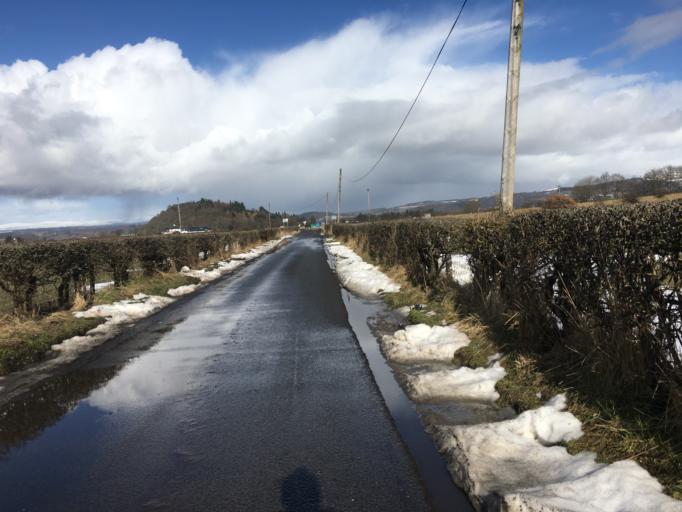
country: GB
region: Scotland
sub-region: Stirling
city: Stirling
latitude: 56.1173
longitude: -3.9742
